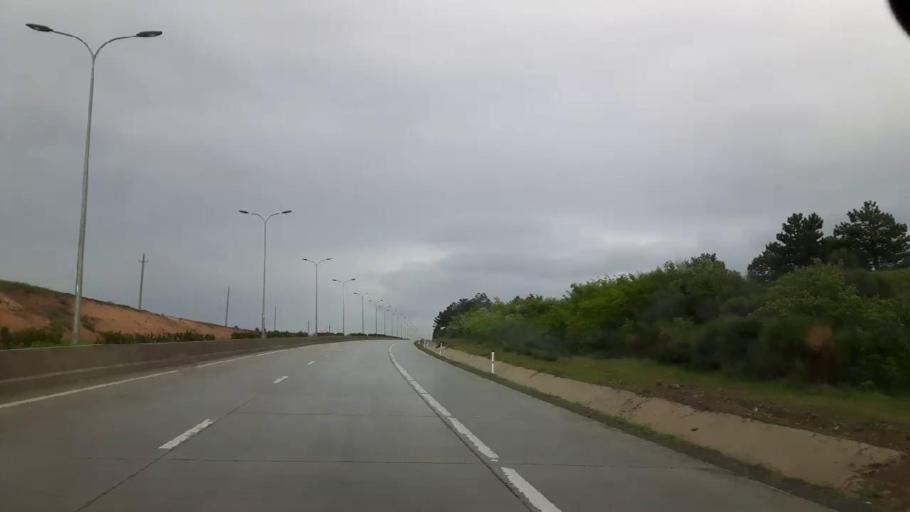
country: GE
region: Shida Kartli
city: Gori
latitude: 42.0187
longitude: 44.0165
